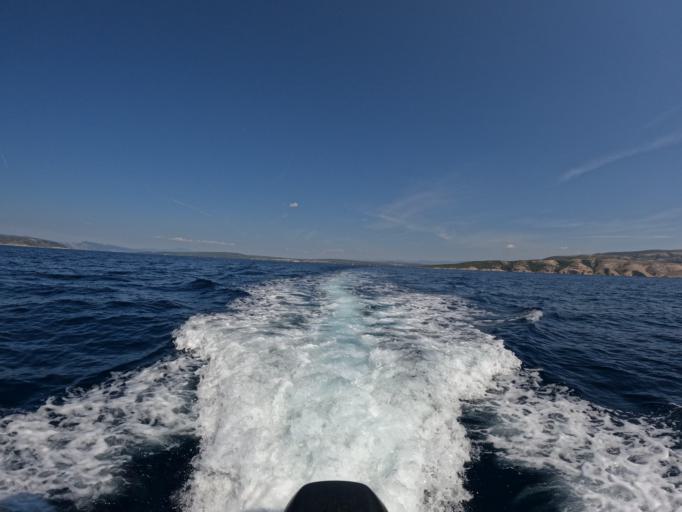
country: HR
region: Primorsko-Goranska
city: Punat
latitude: 44.9505
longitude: 14.6121
